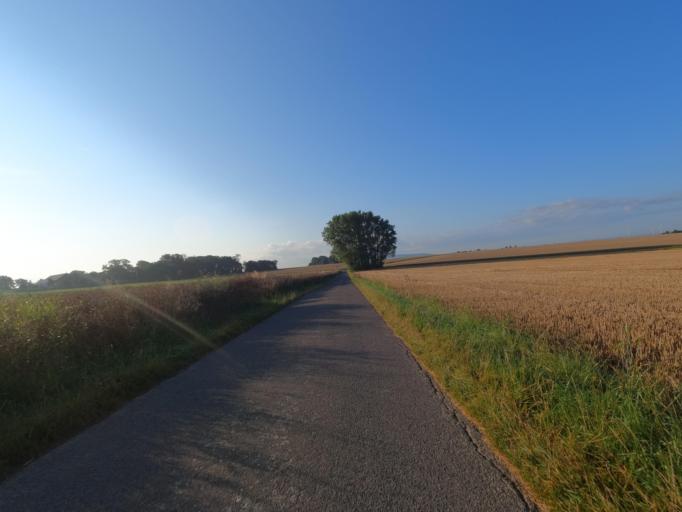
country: DE
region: North Rhine-Westphalia
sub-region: Regierungsbezirk Koln
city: Titz
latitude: 51.0179
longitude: 6.3600
